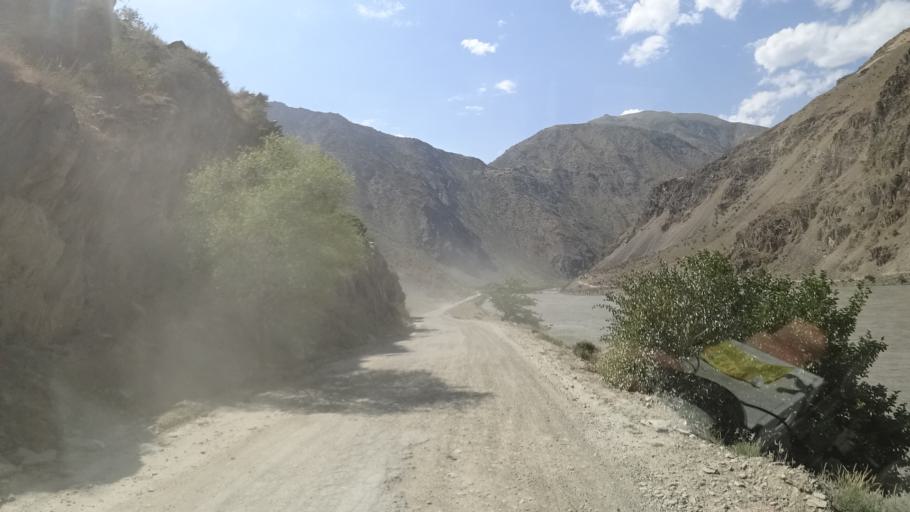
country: AF
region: Badakhshan
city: Maymay
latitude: 38.4599
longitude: 70.9571
